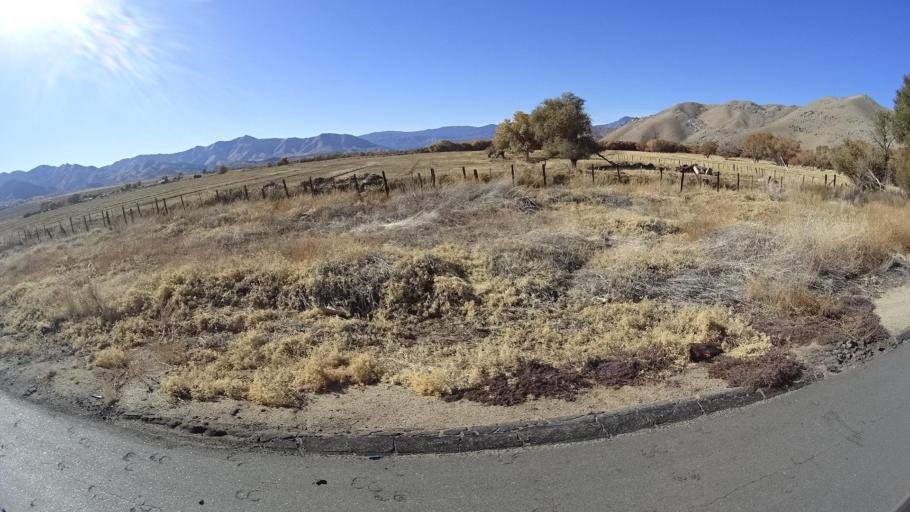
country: US
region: California
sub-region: Kern County
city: Weldon
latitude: 35.6634
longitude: -118.3226
